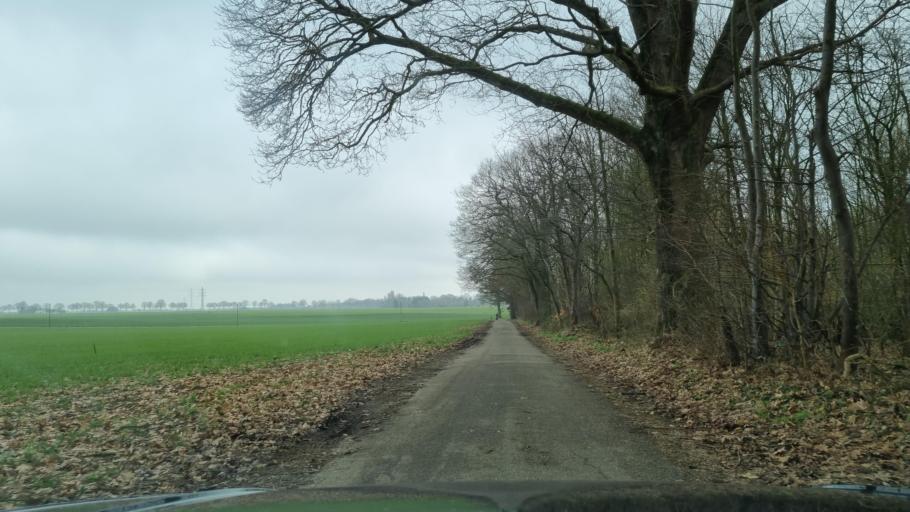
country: DE
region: North Rhine-Westphalia
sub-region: Regierungsbezirk Dusseldorf
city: Kleve
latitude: 51.7620
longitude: 6.1148
